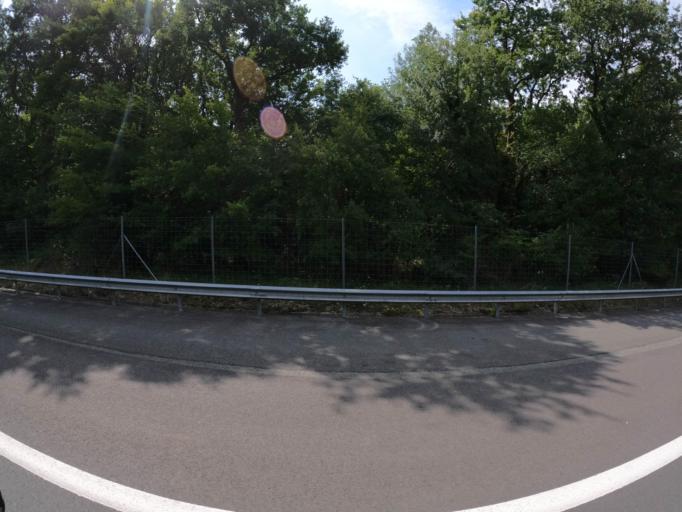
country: FR
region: Poitou-Charentes
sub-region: Departement de la Charente-Maritime
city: Courcon
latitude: 46.2191
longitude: -0.7916
